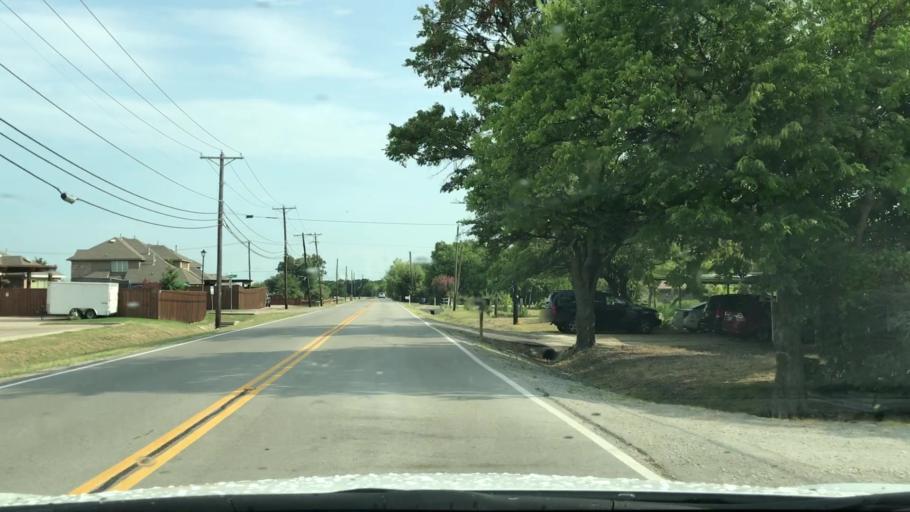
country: US
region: Texas
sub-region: Dallas County
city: Rowlett
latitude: 32.9229
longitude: -96.5352
